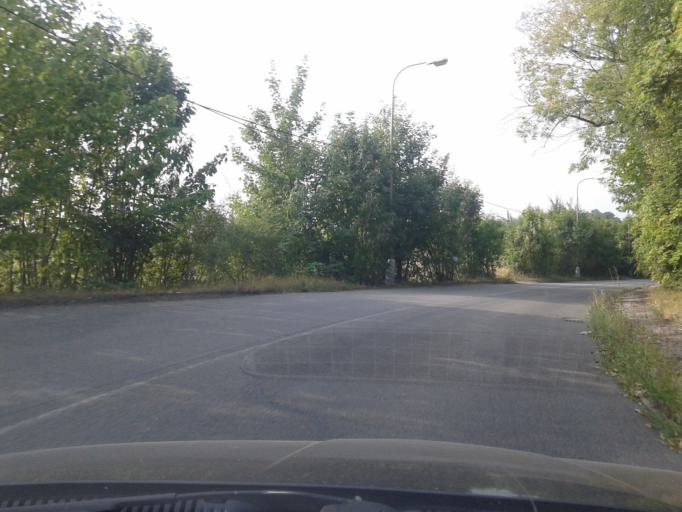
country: CZ
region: Moravskoslezsky
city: Orlova
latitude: 49.8472
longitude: 18.4527
